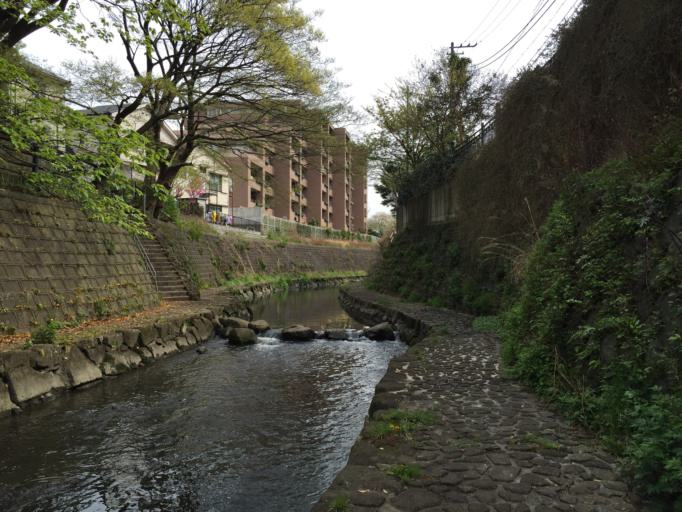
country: JP
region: Kanagawa
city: Yokohama
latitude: 35.4065
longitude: 139.5930
